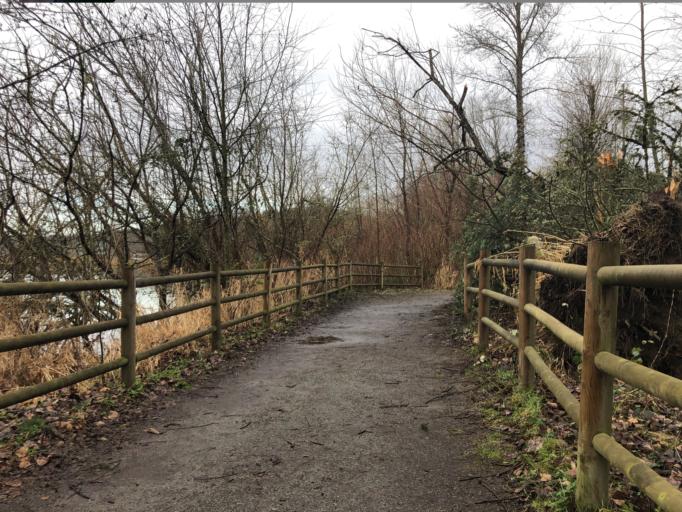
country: US
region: Washington
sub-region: King County
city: West Lake Sammamish
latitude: 47.5605
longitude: -122.0647
